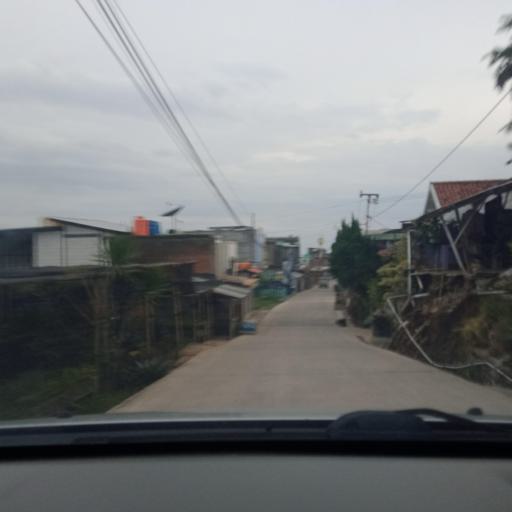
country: ID
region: West Java
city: Lembang
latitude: -6.8334
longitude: 107.5858
